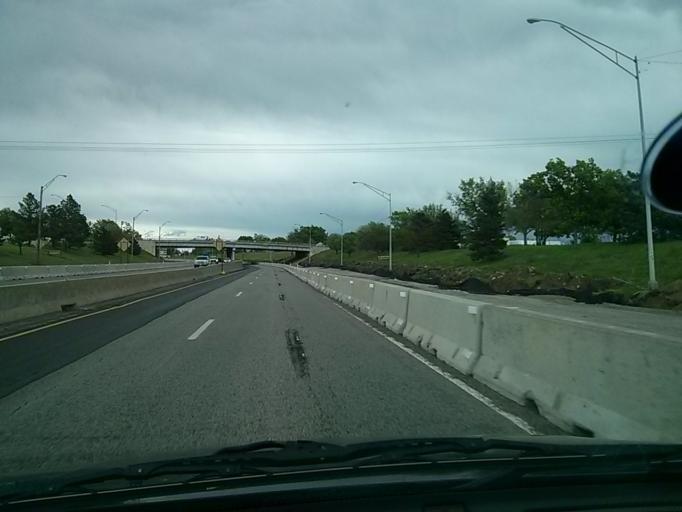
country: US
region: Oklahoma
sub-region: Tulsa County
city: Tulsa
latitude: 36.1591
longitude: -95.9700
